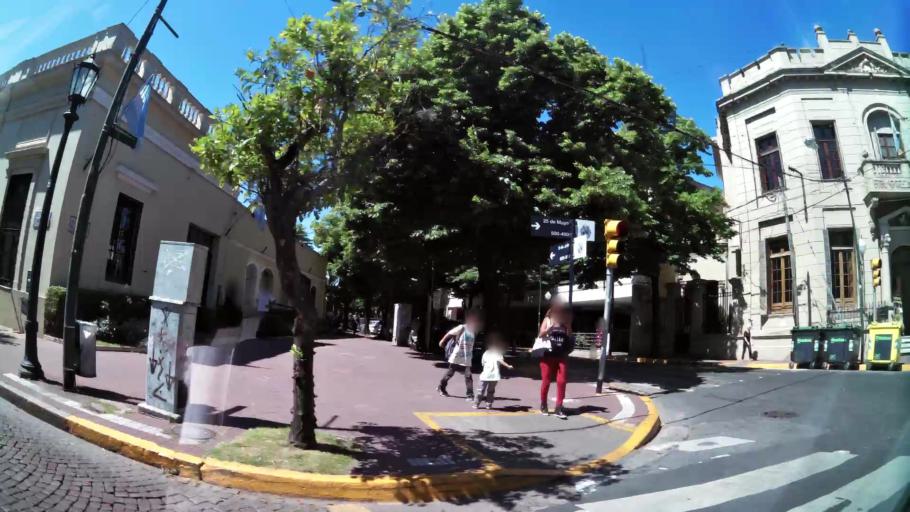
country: AR
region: Buenos Aires
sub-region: Partido de San Isidro
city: San Isidro
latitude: -34.4682
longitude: -58.5106
